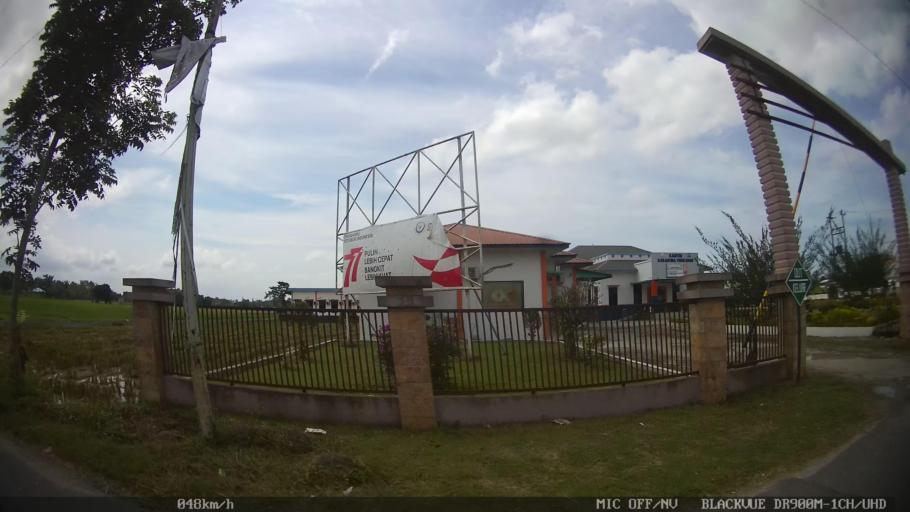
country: ID
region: North Sumatra
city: Percut
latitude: 3.6108
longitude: 98.8454
